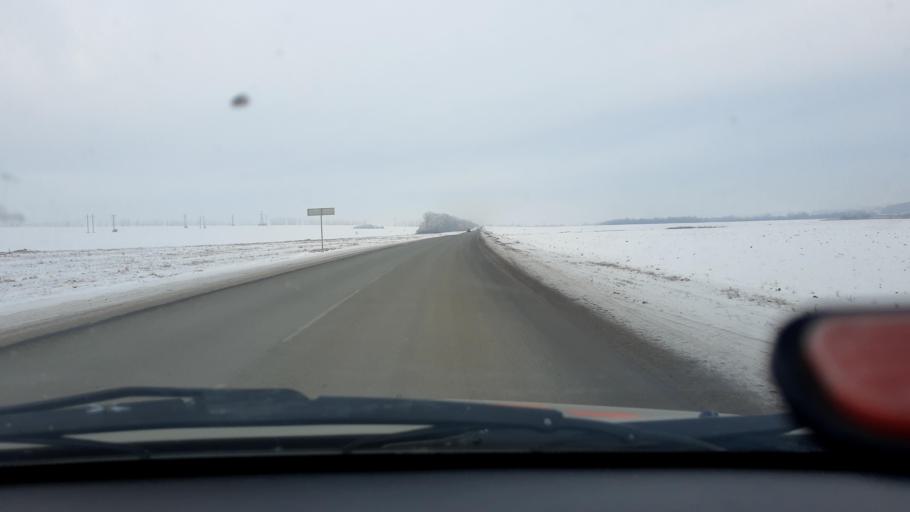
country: RU
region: Bashkortostan
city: Avdon
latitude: 54.3846
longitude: 55.8055
